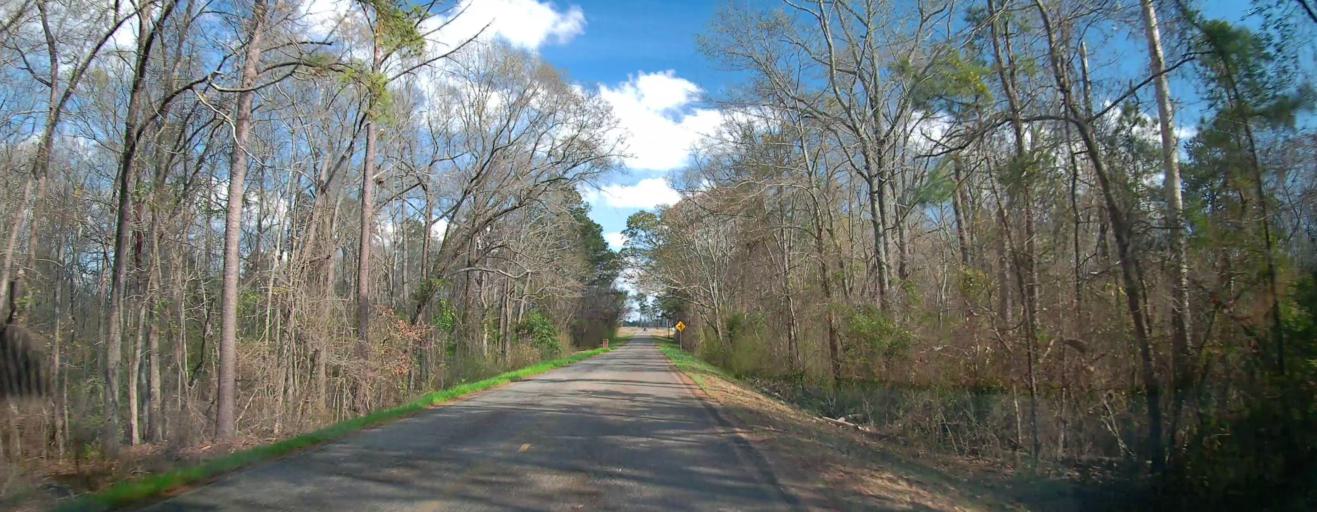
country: US
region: Georgia
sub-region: Wilkinson County
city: Irwinton
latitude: 32.6385
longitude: -83.1593
